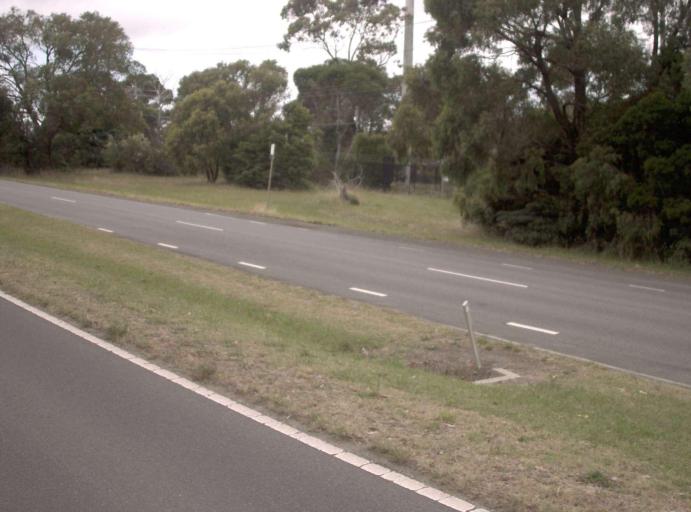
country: AU
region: Victoria
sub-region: Cardinia
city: Pakenham Upper
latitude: -38.0702
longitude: 145.4935
